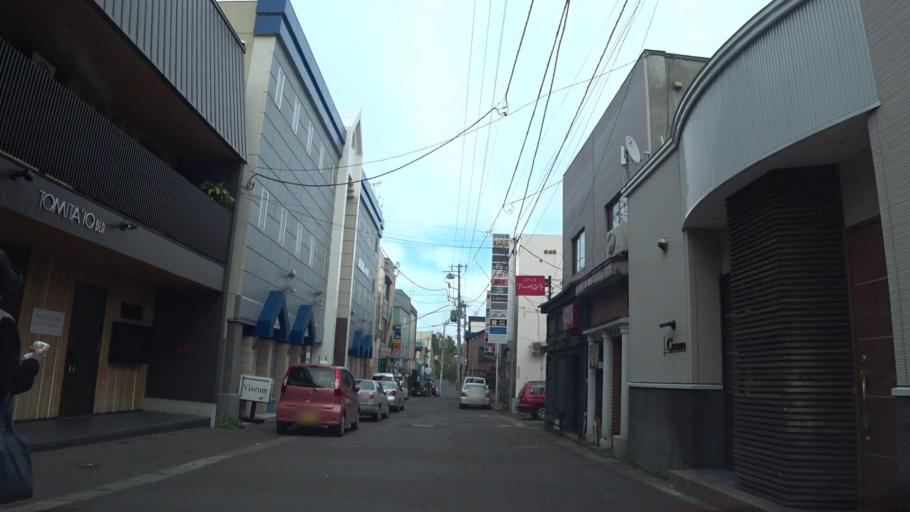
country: JP
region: Hokkaido
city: Otaru
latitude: 43.1921
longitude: 140.9991
